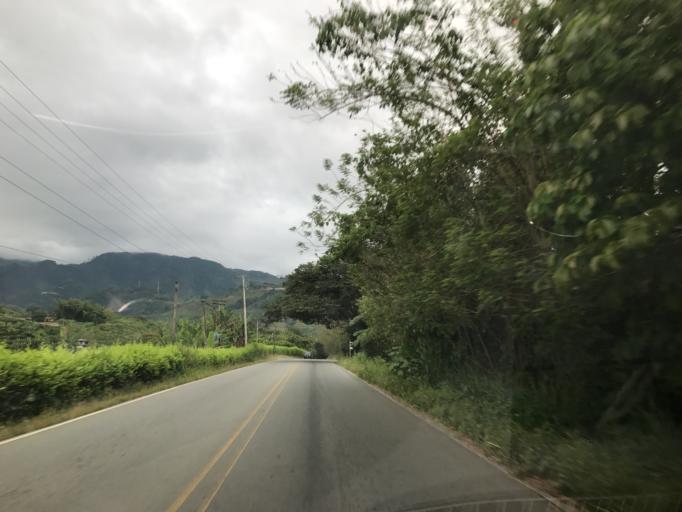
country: CO
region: Quindio
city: Buenavista
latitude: 4.3829
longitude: -75.7561
